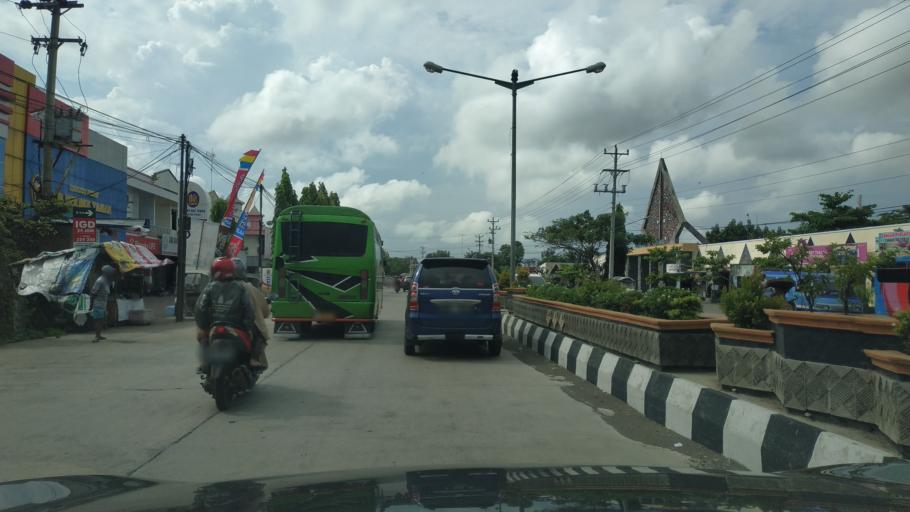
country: ID
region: Central Java
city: Pemalang
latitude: -6.9057
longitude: 109.3832
